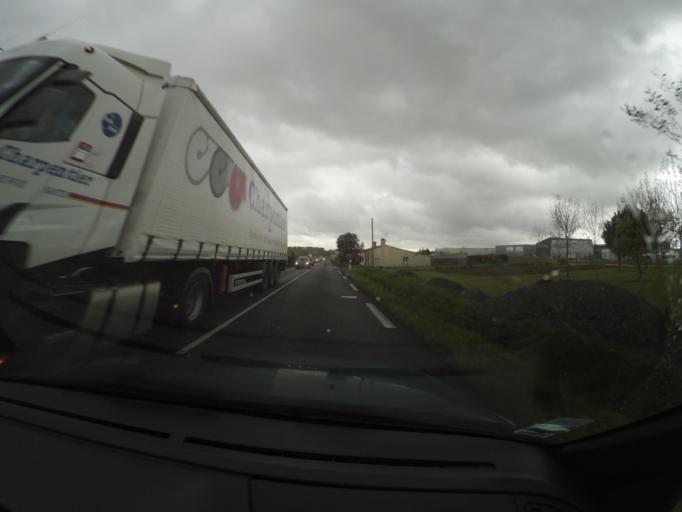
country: FR
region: Pays de la Loire
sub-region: Departement de la Loire-Atlantique
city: Vallet
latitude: 47.1824
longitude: -1.2575
